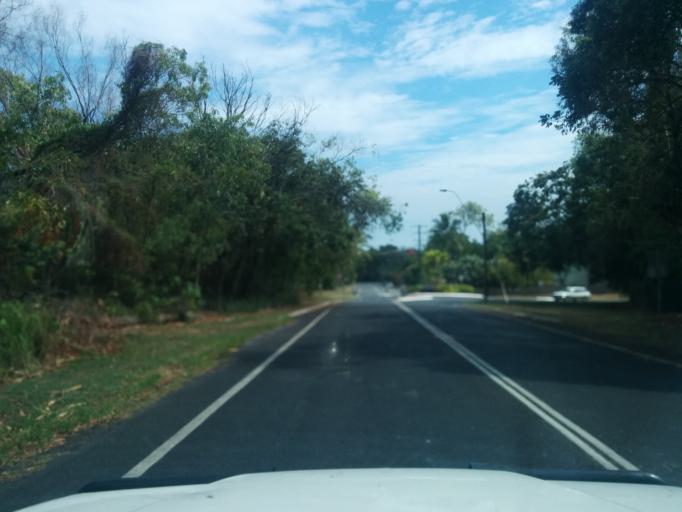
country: AU
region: Queensland
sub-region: Cairns
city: Yorkeys Knob
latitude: -16.8427
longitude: 145.7353
